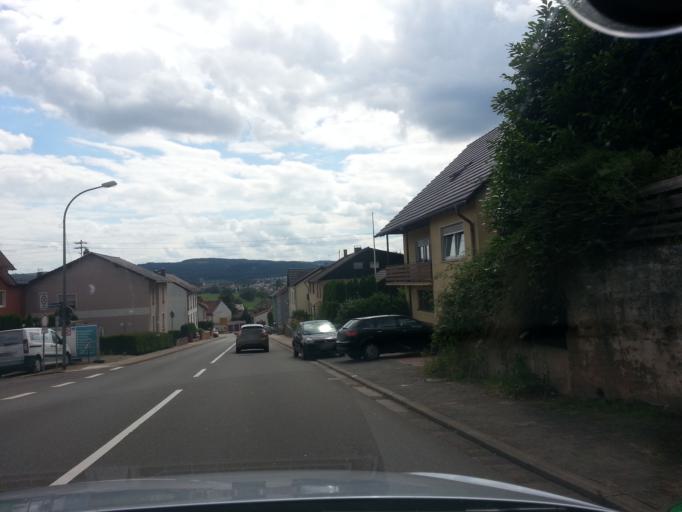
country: DE
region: Saarland
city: Mettlach
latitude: 49.4799
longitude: 6.6025
